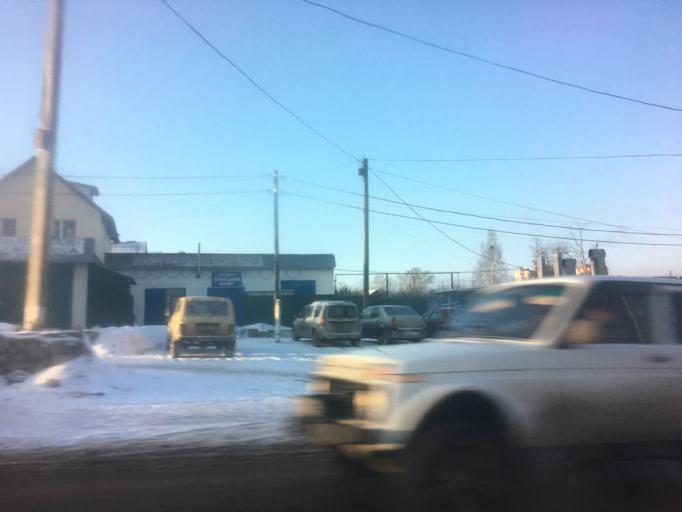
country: RU
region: Tula
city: Tula
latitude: 54.2024
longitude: 37.6807
